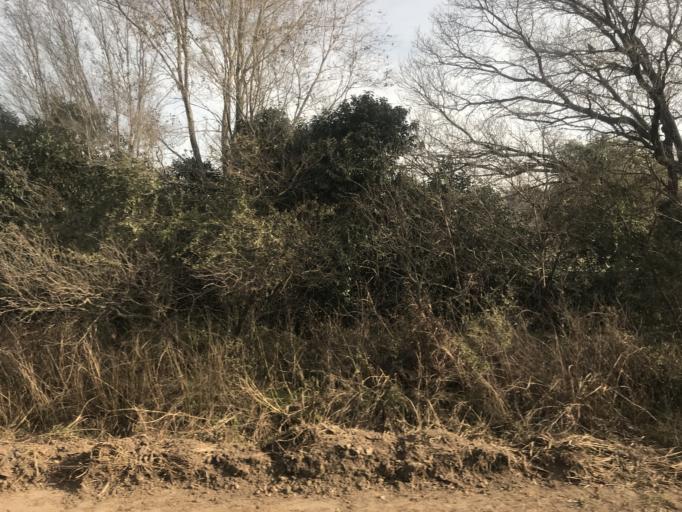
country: AR
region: Cordoba
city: Laguna Larga
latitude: -31.7825
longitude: -63.7983
